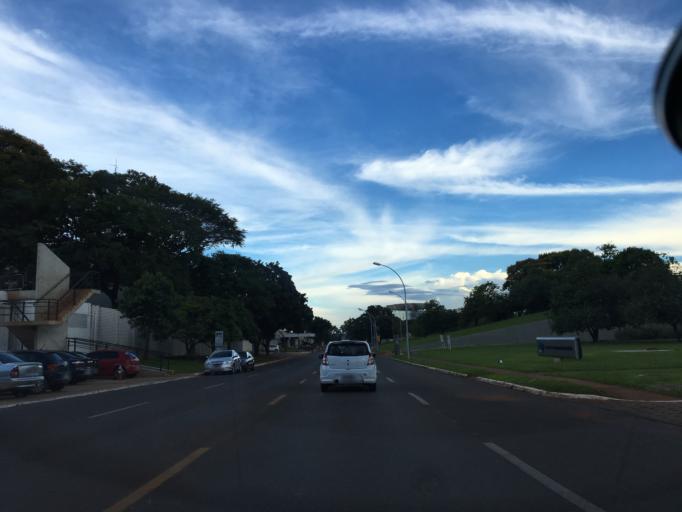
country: BR
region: Federal District
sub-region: Brasilia
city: Brasilia
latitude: -15.8023
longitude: -47.8631
